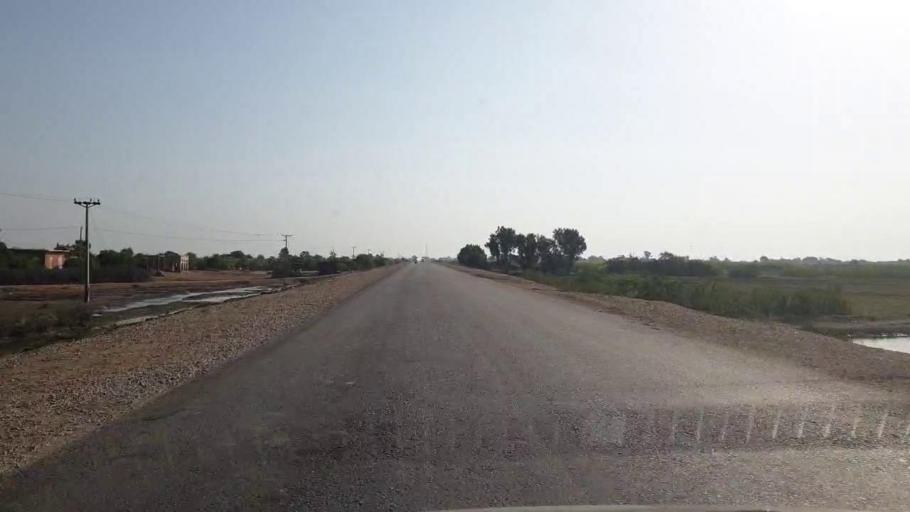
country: PK
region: Sindh
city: Badin
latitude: 24.6590
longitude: 68.9302
